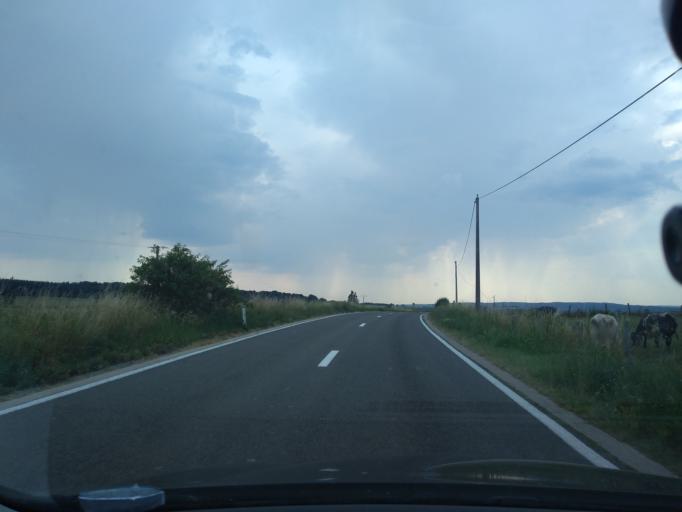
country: BE
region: Wallonia
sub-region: Province du Luxembourg
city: Bertogne
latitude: 50.0820
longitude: 5.6990
